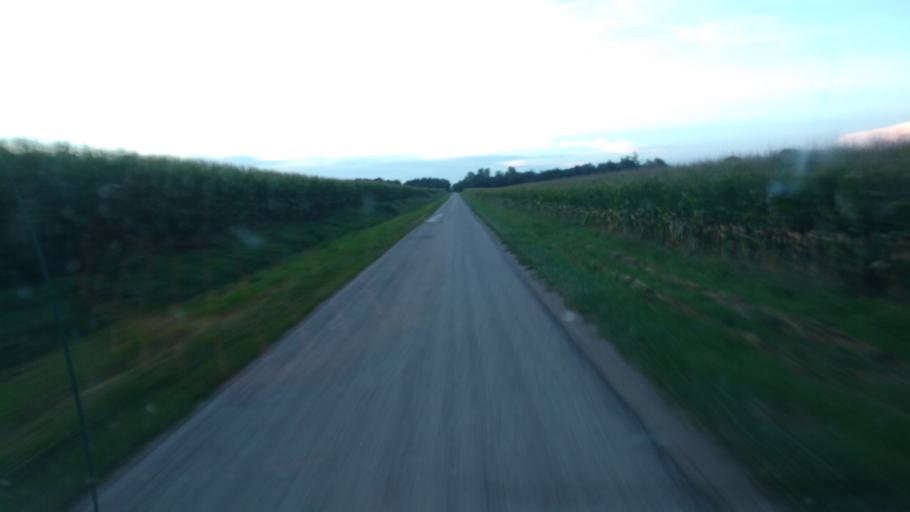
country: US
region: Ohio
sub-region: Crawford County
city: Galion
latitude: 40.6991
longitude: -82.8655
